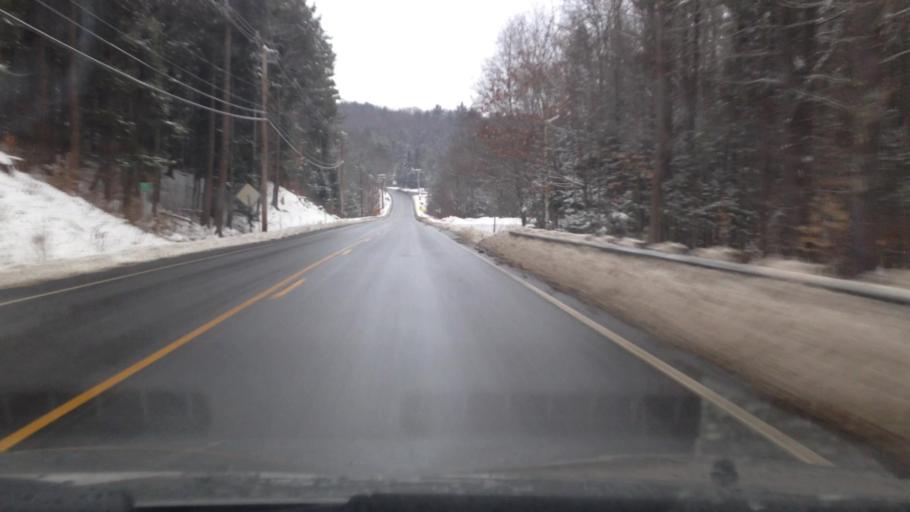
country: US
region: New Hampshire
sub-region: Cheshire County
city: Keene
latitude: 43.0423
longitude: -72.2675
